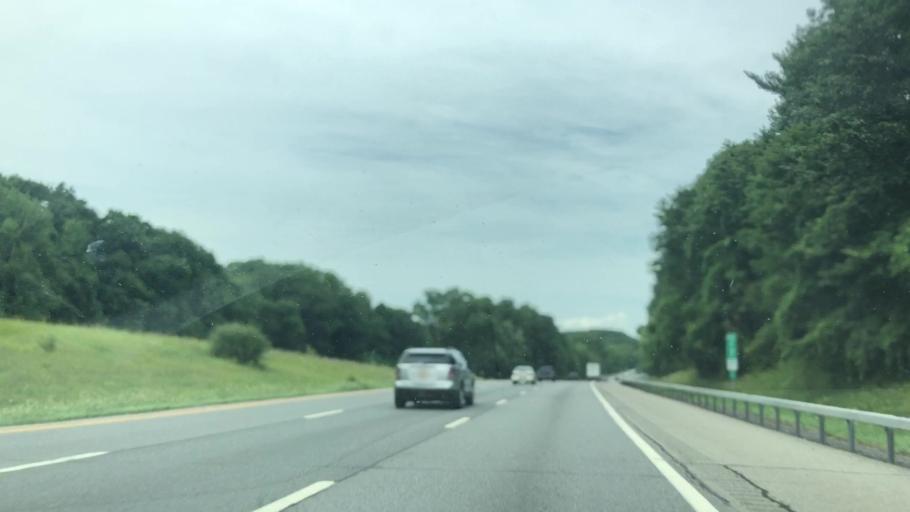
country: US
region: New York
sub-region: Saratoga County
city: Country Knolls
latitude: 42.9230
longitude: -73.8009
